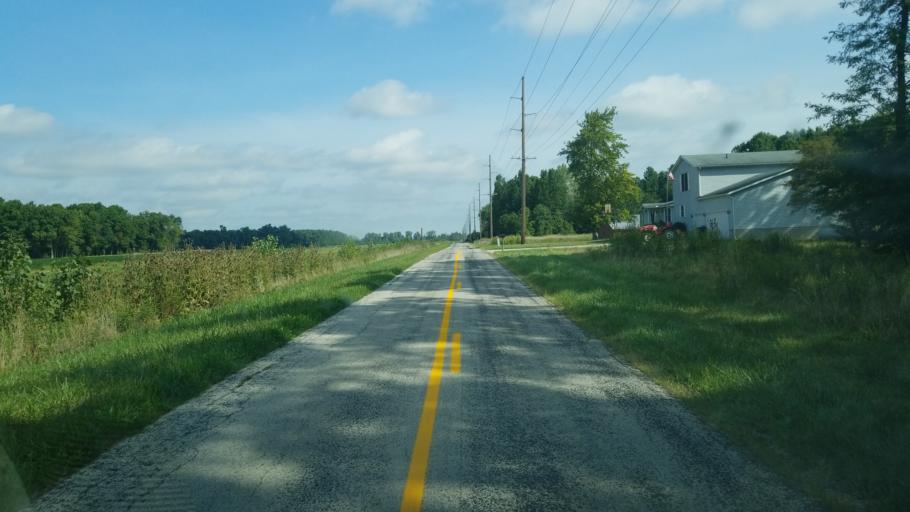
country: US
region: Ohio
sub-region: Wyandot County
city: Upper Sandusky
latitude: 40.6759
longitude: -83.3241
